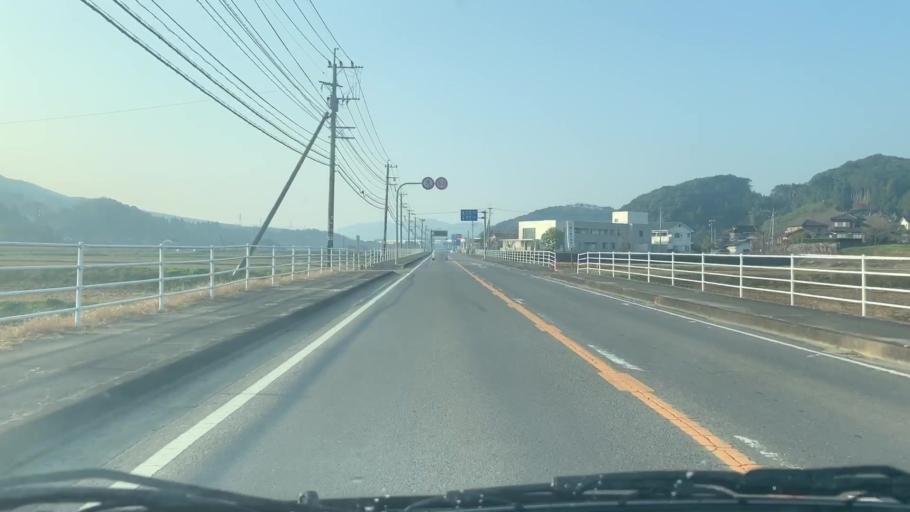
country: JP
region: Saga Prefecture
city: Takeocho-takeo
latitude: 33.1603
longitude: 130.0002
